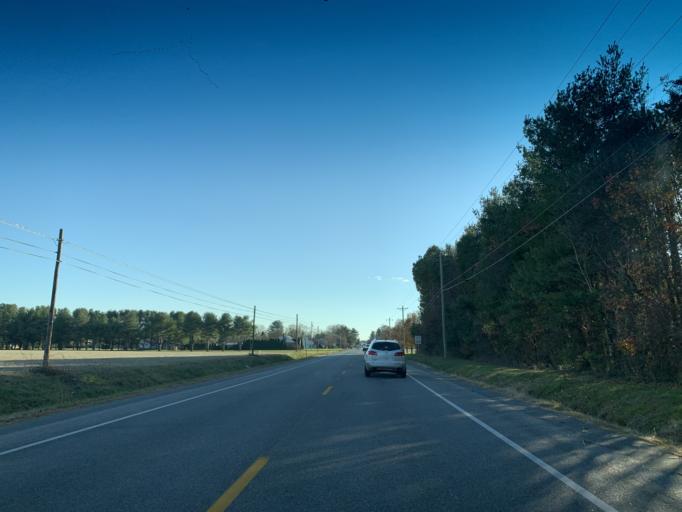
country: US
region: Delaware
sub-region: New Castle County
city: Middletown
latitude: 39.3515
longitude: -75.8777
